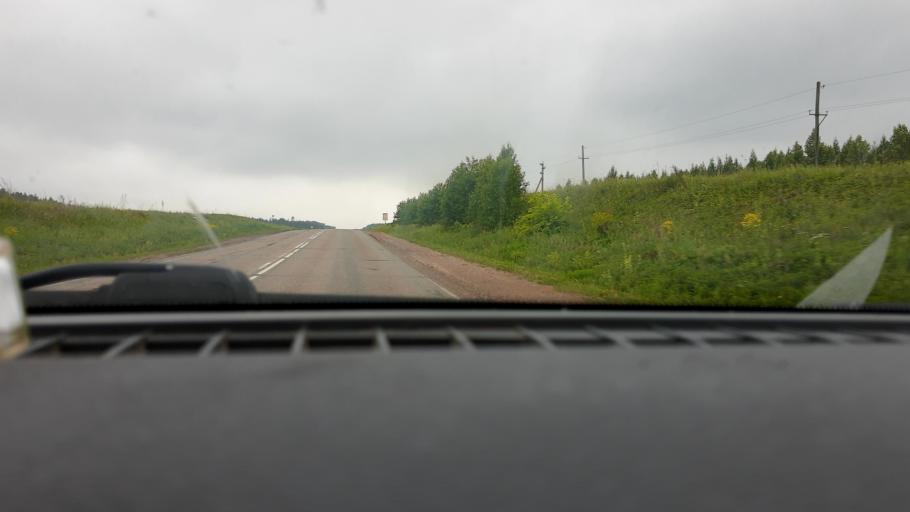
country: RU
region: Bashkortostan
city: Belebey
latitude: 54.2348
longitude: 54.0729
